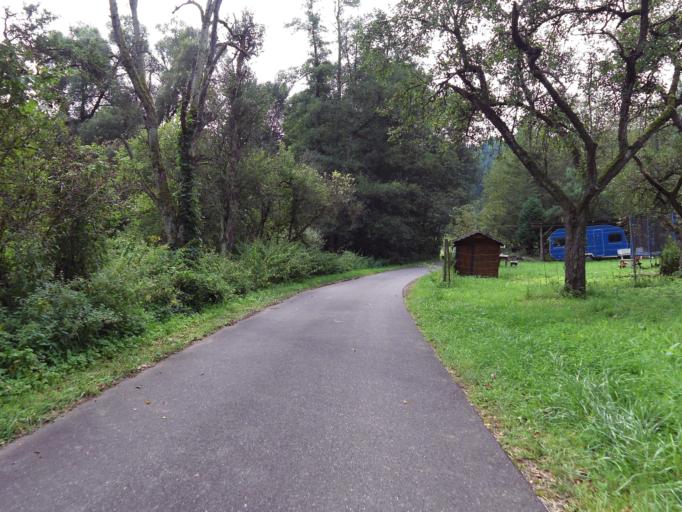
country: DE
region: Rheinland-Pfalz
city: Hochstatten
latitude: 49.7724
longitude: 7.8307
